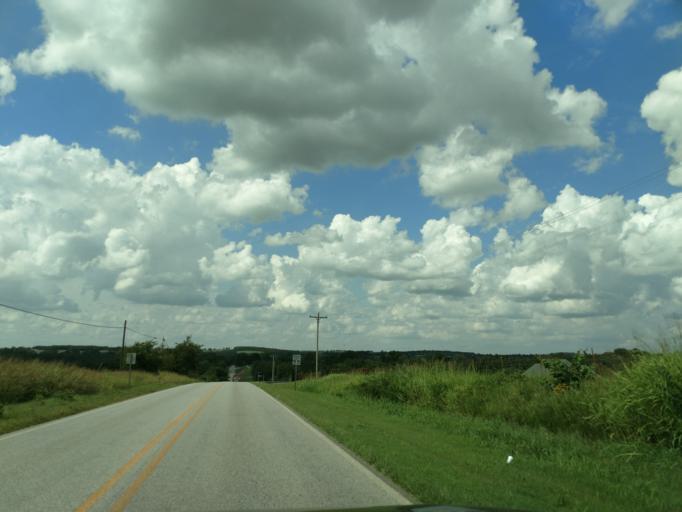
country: US
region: Arkansas
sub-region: Carroll County
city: Berryville
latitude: 36.3965
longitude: -93.5661
